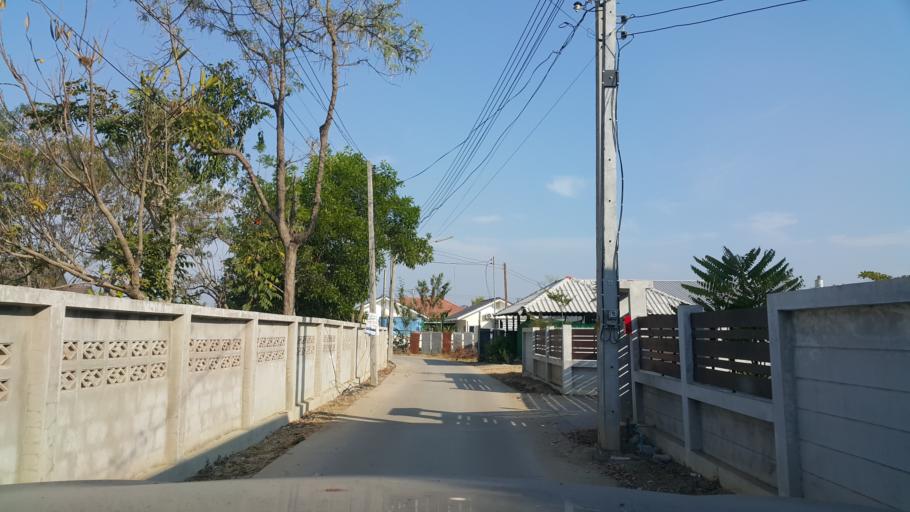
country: TH
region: Chiang Mai
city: San Sai
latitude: 18.8345
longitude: 99.0884
